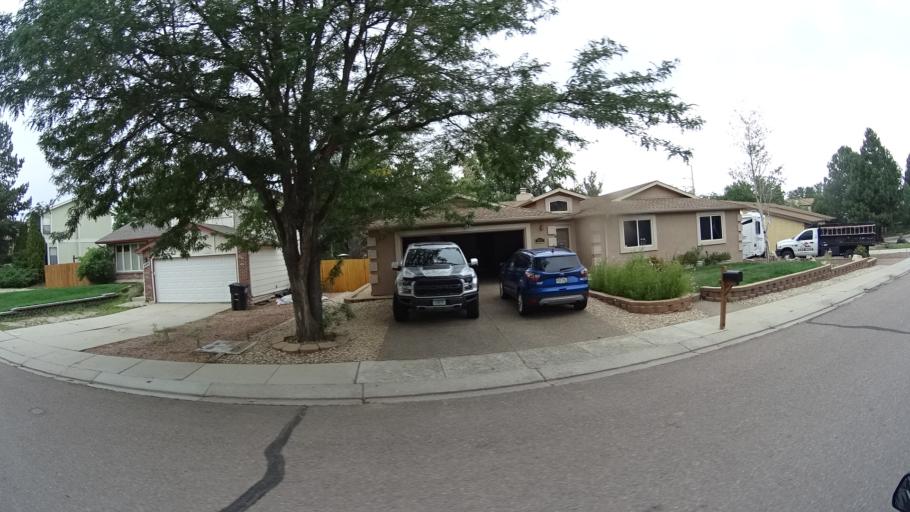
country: US
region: Colorado
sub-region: El Paso County
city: Air Force Academy
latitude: 38.9241
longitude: -104.8096
